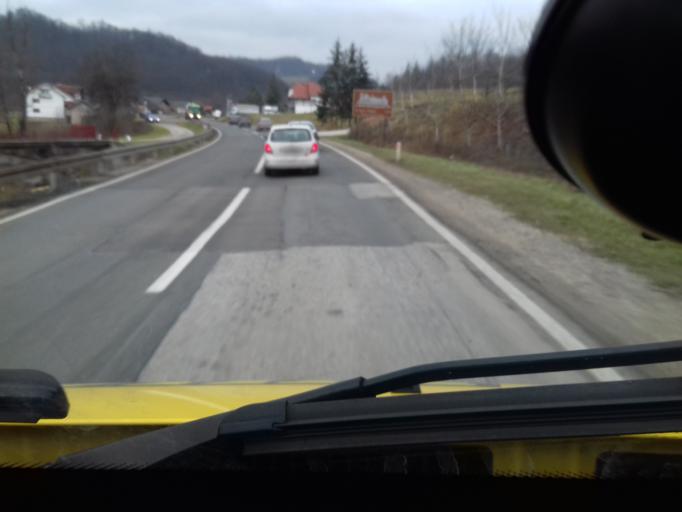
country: BA
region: Federation of Bosnia and Herzegovina
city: Lijesnica
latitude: 44.4926
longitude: 18.0846
